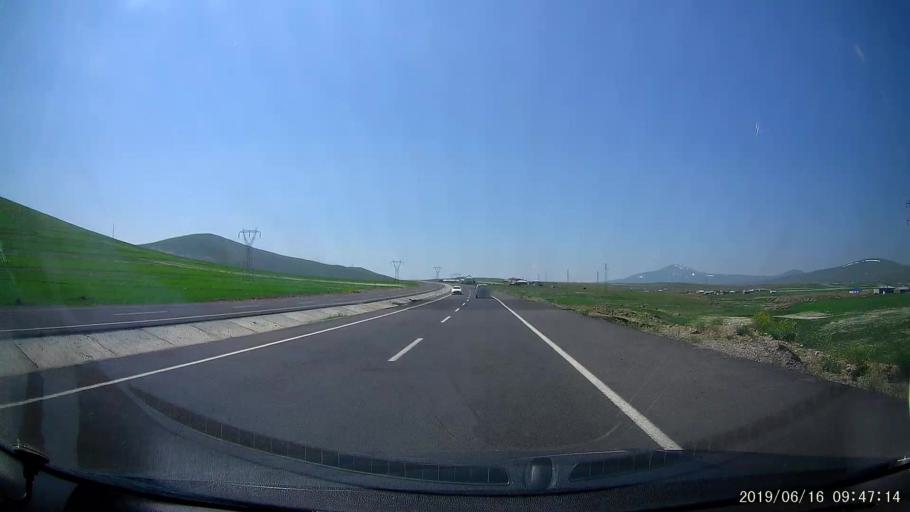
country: TR
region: Kars
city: Digor
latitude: 40.4513
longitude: 43.3421
